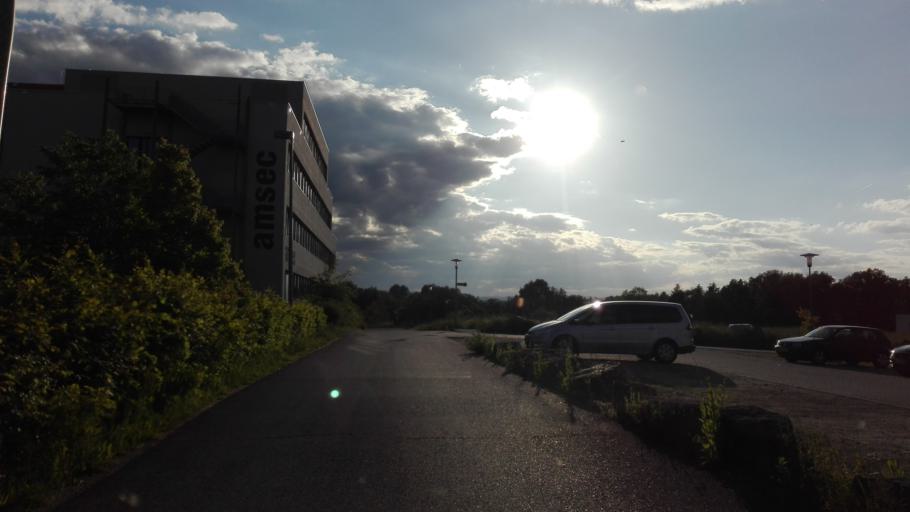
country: AT
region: Upper Austria
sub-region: Politischer Bezirk Urfahr-Umgebung
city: Engerwitzdorf
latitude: 48.3698
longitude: 14.5139
